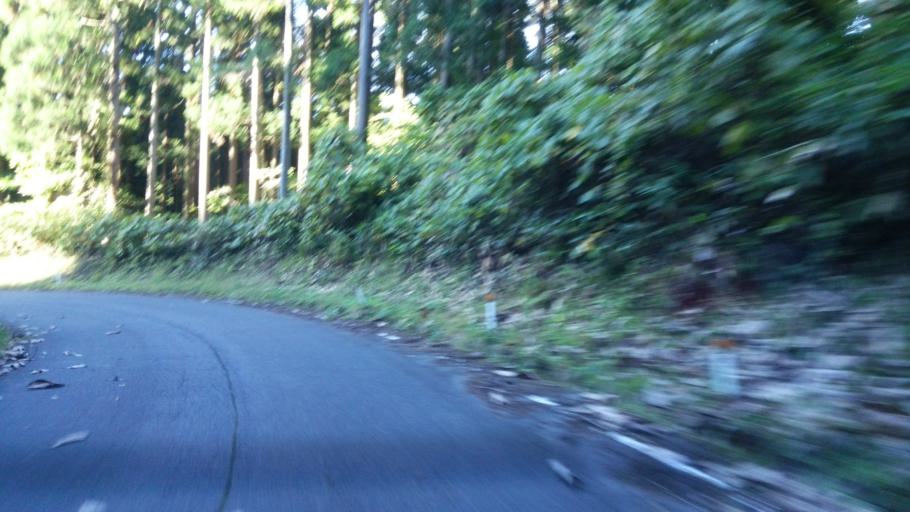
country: JP
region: Fukushima
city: Kitakata
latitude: 37.4469
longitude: 139.7183
